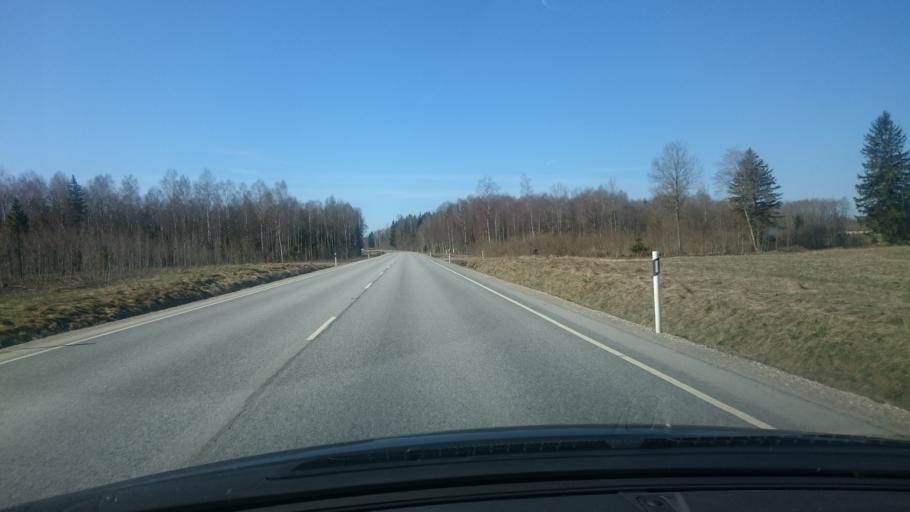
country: EE
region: Raplamaa
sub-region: Rapla vald
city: Rapla
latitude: 59.0272
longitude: 24.8172
